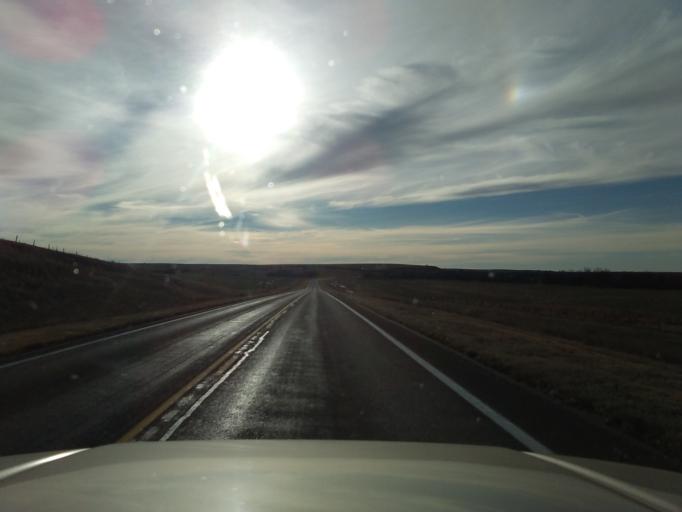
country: US
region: Kansas
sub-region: Norton County
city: Norton
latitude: 39.7283
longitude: -100.1833
